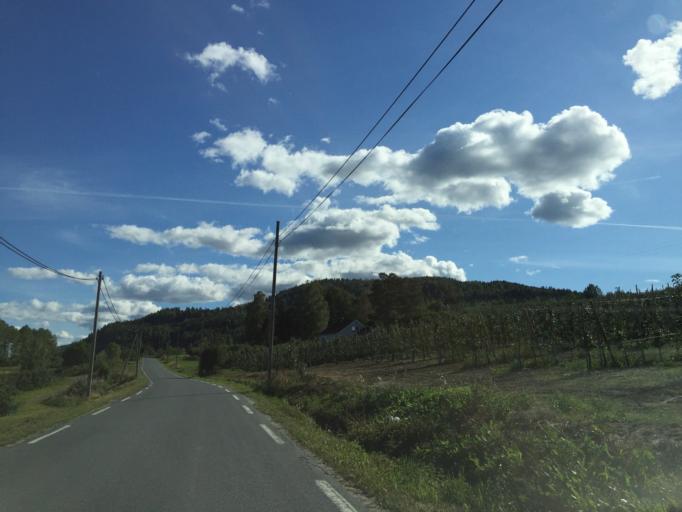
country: NO
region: Buskerud
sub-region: Ovre Eiker
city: Hokksund
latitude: 59.6918
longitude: 9.8454
